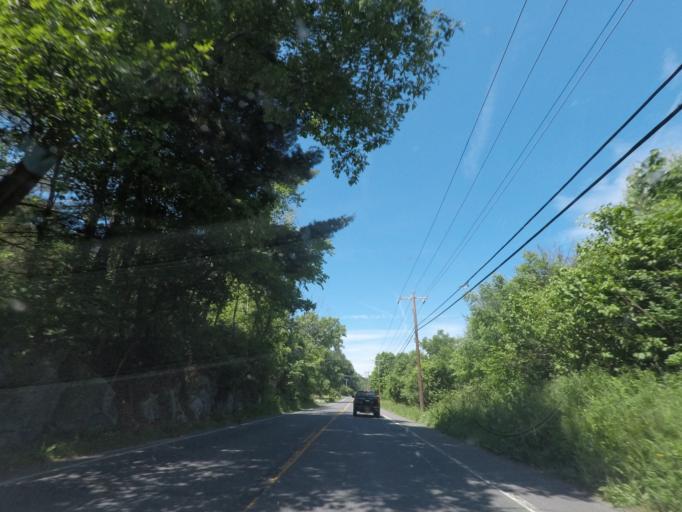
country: US
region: Massachusetts
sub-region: Berkshire County
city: Great Barrington
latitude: 42.1999
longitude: -73.5092
